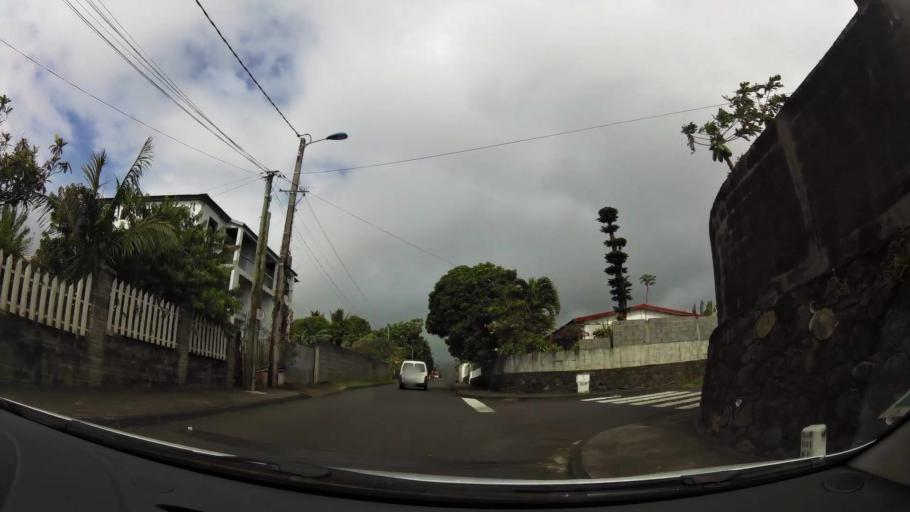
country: RE
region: Reunion
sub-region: Reunion
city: Sainte-Marie
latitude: -20.8996
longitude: 55.5575
